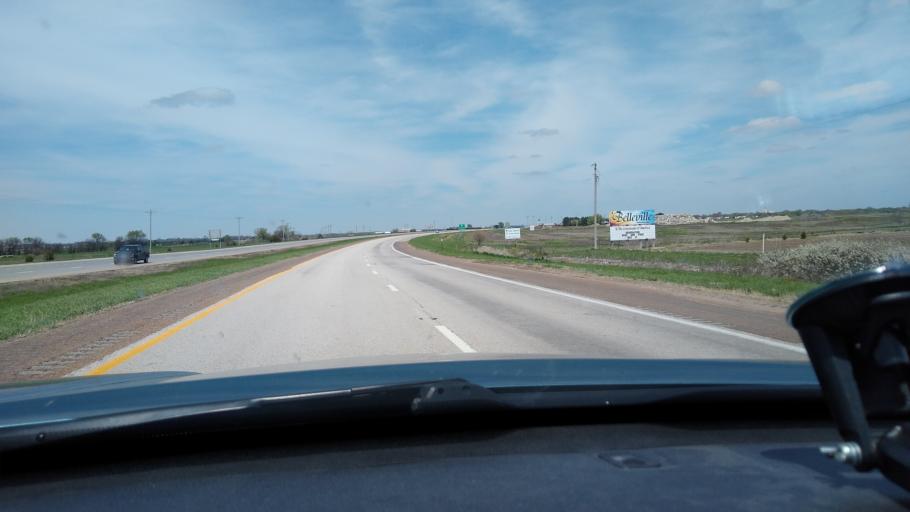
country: US
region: Kansas
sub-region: Republic County
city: Belleville
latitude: 39.8011
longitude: -97.6519
